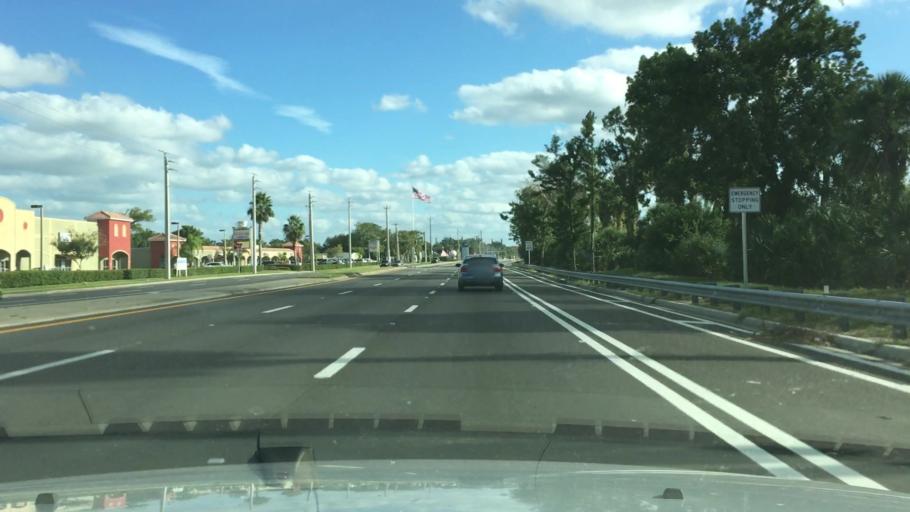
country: US
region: Florida
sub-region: Volusia County
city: Holly Hill
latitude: 29.2268
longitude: -81.0508
